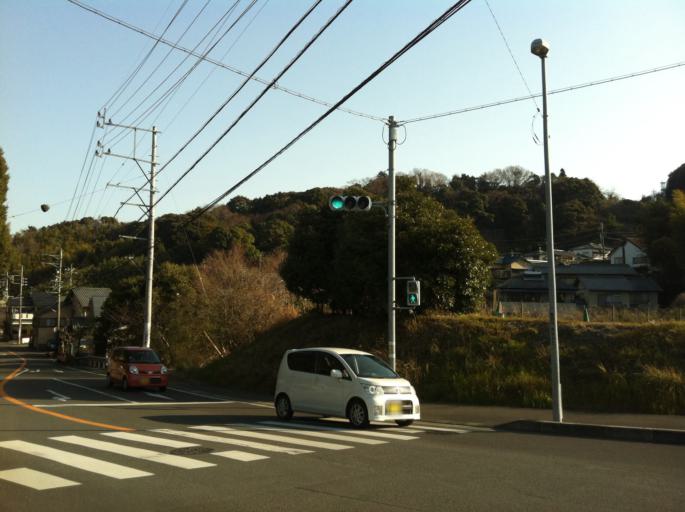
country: JP
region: Shizuoka
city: Shizuoka-shi
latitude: 34.9935
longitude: 138.4533
